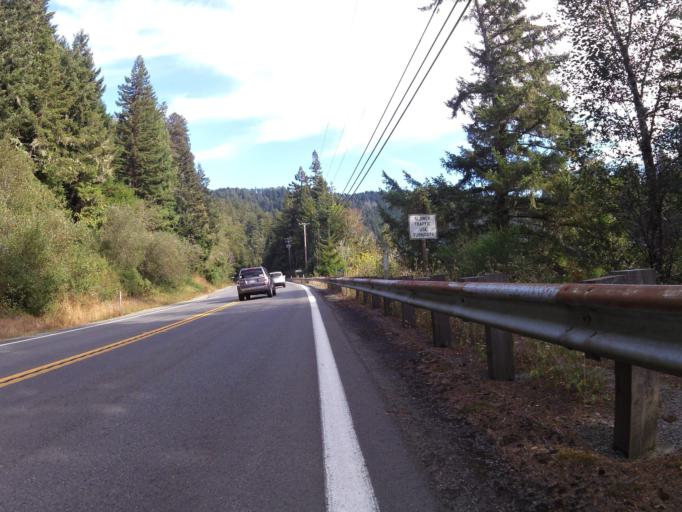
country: US
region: California
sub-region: Del Norte County
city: Bertsch-Oceanview
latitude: 41.8150
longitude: -124.0874
